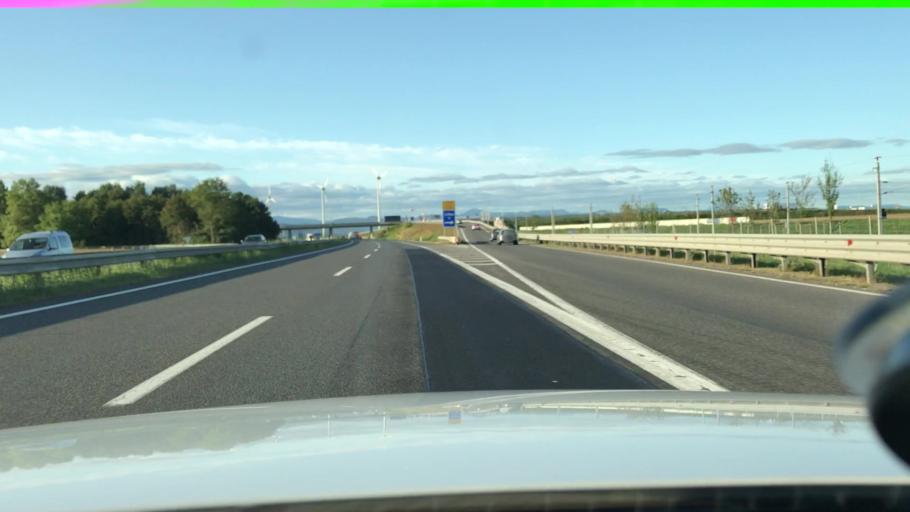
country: AT
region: Lower Austria
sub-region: Sankt Polten Stadt
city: Sankt Poelten
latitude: 48.2027
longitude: 15.6631
